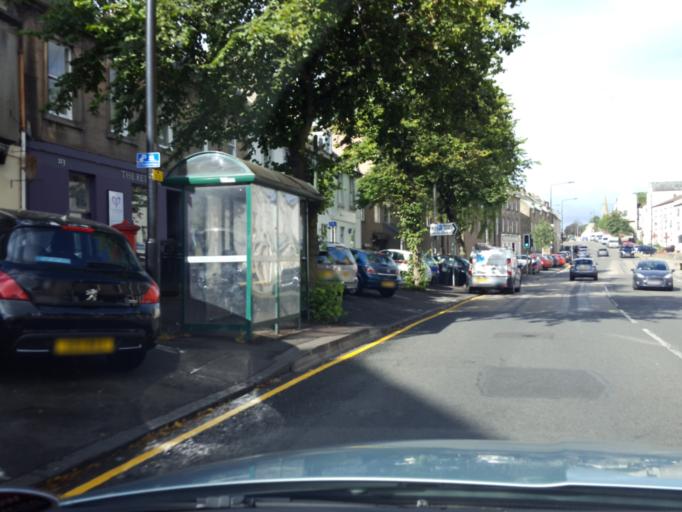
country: GB
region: Scotland
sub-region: West Lothian
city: Linlithgow
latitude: 55.9760
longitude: -3.6056
